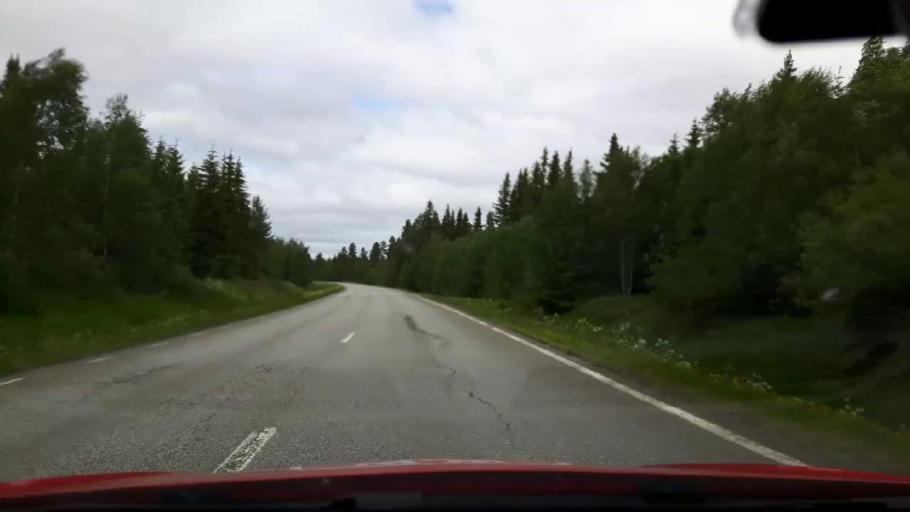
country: SE
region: Jaemtland
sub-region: Krokoms Kommun
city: Krokom
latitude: 63.4319
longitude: 14.4990
